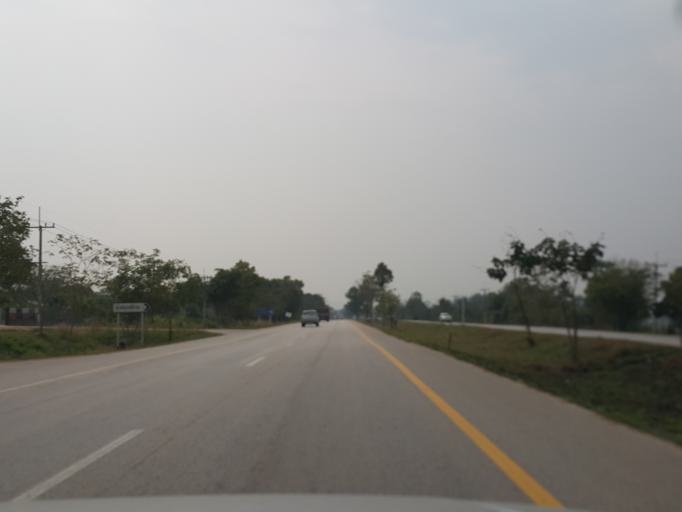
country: TH
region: Lampang
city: Ko Kha
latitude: 18.1693
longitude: 99.4064
